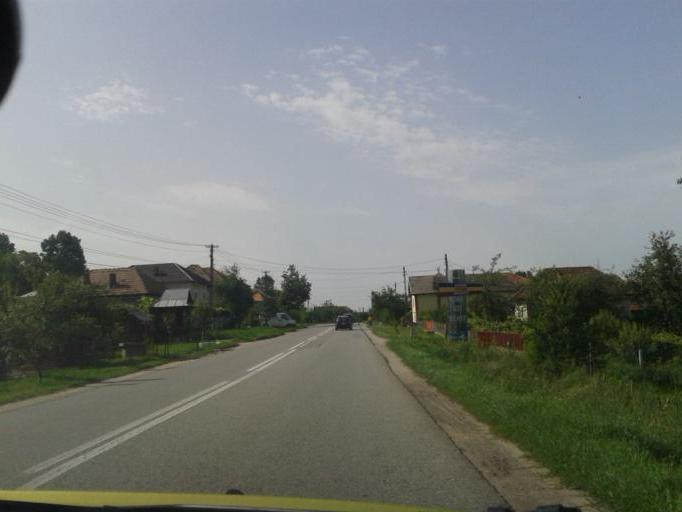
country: RO
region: Valcea
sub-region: Comuna Barbatesti
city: Bodesti
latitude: 45.1219
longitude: 24.1156
